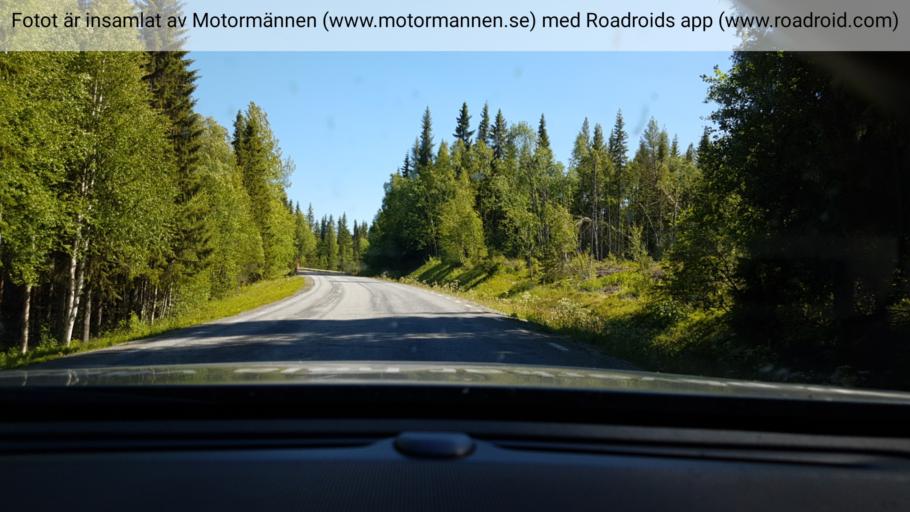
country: SE
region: Vaesterbotten
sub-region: Vilhelmina Kommun
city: Sjoberg
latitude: 64.6597
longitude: 16.3138
